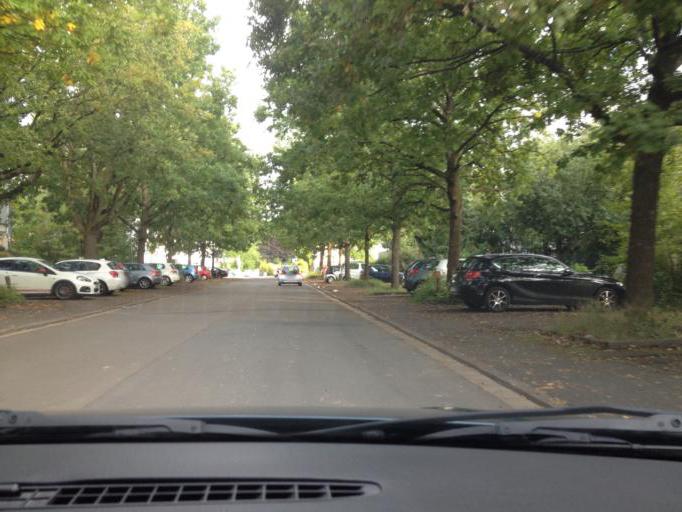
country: DE
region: Saarland
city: Sankt Wendel
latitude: 49.4657
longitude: 7.1737
